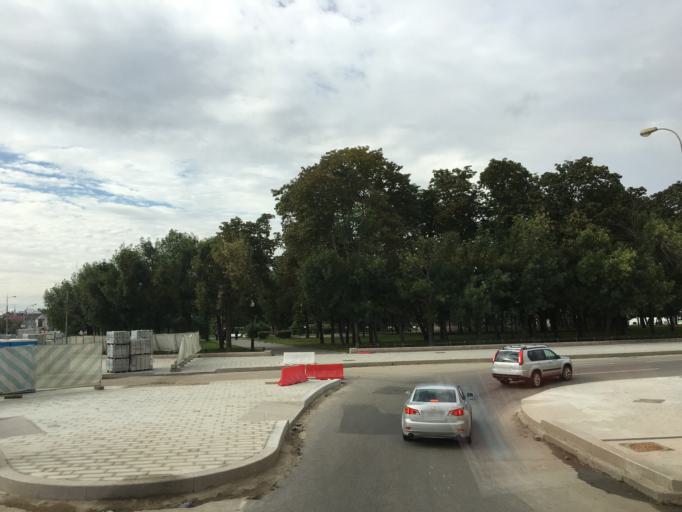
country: RU
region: Moscow
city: Moscow
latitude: 55.7459
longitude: 37.6210
